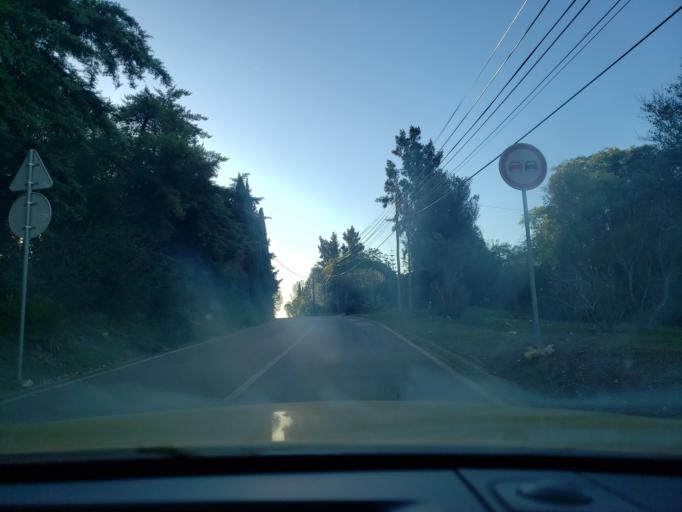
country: PT
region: Faro
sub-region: Portimao
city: Alvor
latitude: 37.1852
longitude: -8.5862
